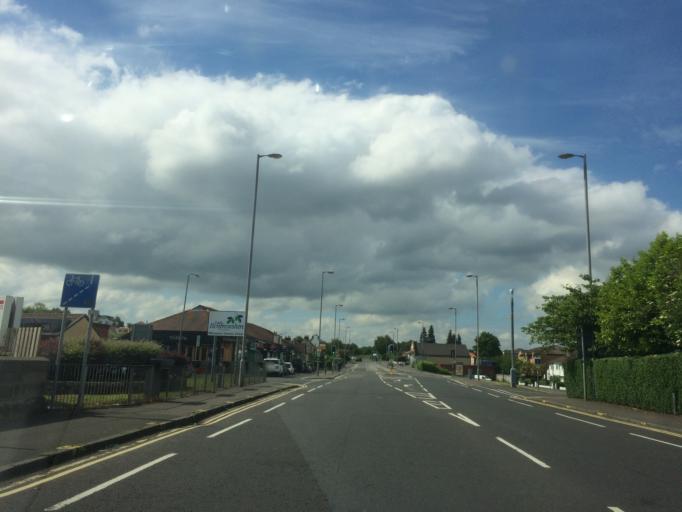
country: GB
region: Scotland
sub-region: East Renfrewshire
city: Giffnock
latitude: 55.8134
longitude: -4.2914
